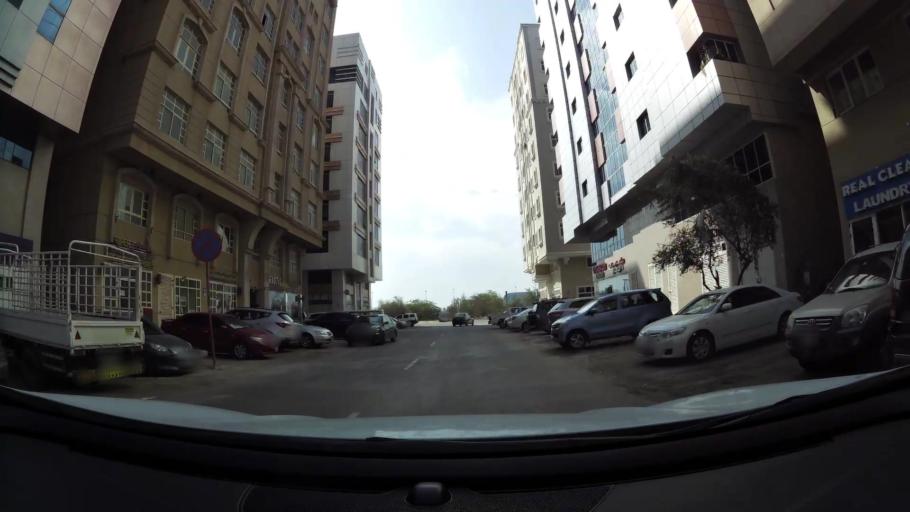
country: AE
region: Abu Dhabi
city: Abu Dhabi
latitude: 24.3410
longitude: 54.5315
